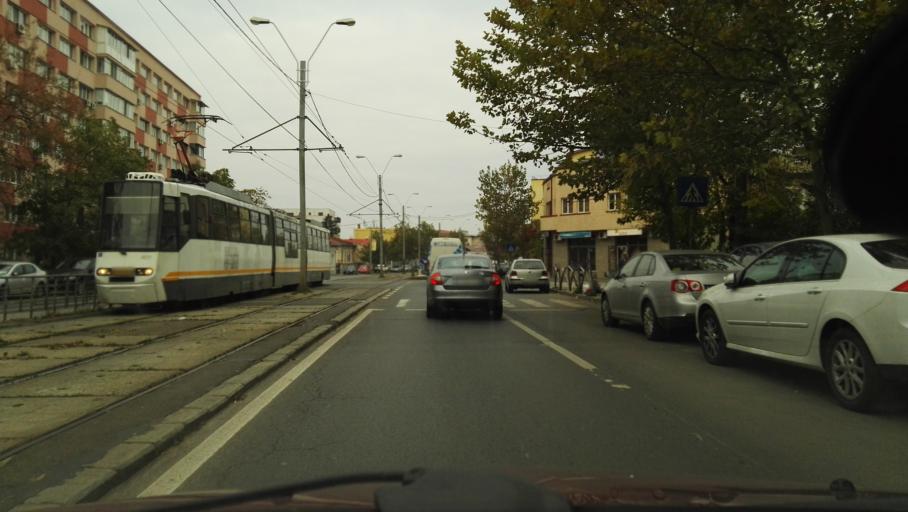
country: RO
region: Bucuresti
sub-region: Municipiul Bucuresti
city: Bucuresti
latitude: 44.4078
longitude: 26.0920
